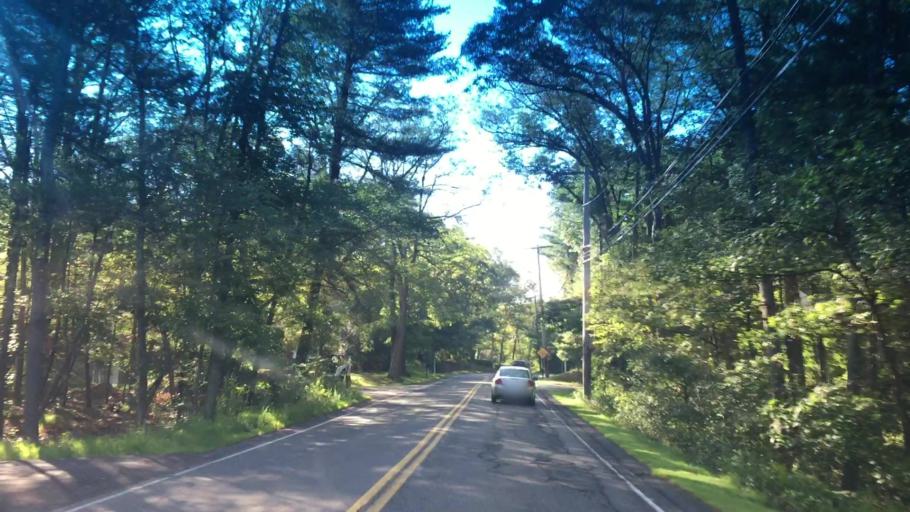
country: US
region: Massachusetts
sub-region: Norfolk County
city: Norfolk
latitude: 42.1326
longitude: -71.3386
